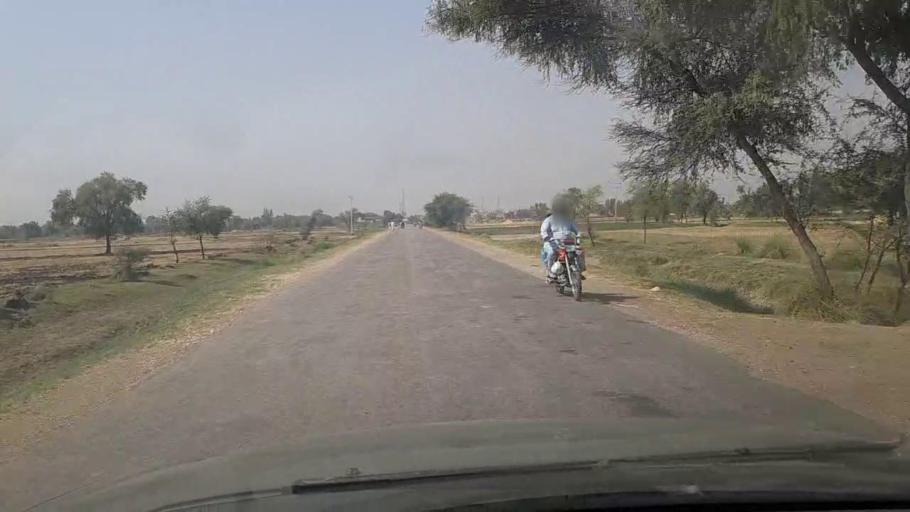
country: PK
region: Sindh
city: Mirpur Mathelo
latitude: 27.9234
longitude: 69.5278
